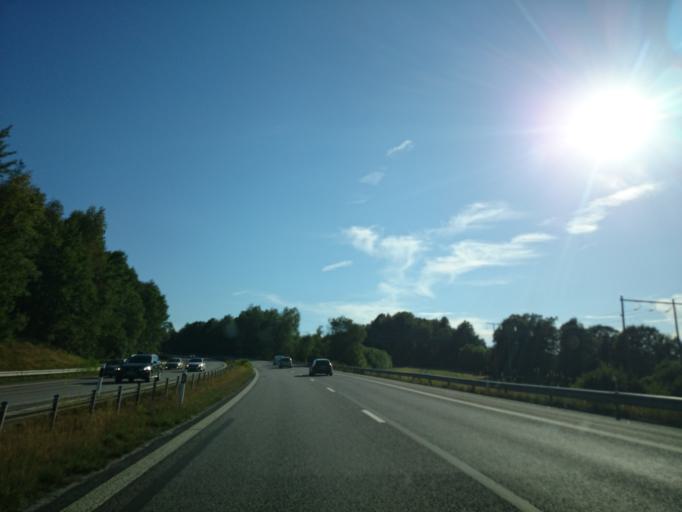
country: SE
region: Soedermanland
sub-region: Nykopings Kommun
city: Nykoping
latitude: 58.7684
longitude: 16.9973
